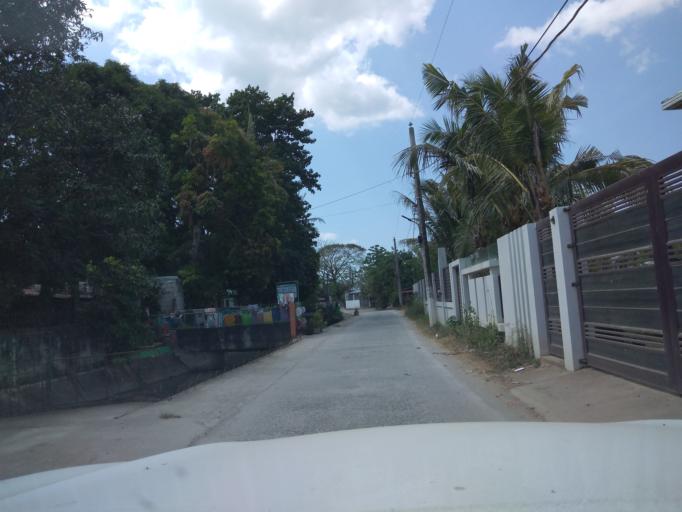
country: PH
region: Central Luzon
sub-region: Province of Pampanga
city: Bahay Pare
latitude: 15.0350
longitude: 120.8732
